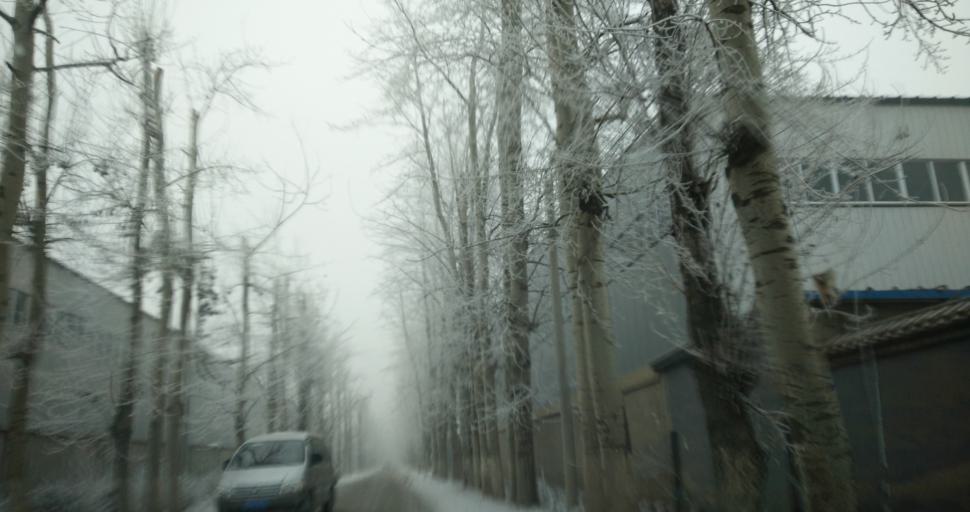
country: CN
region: Beijing
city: Yinghai
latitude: 39.7092
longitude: 116.4286
